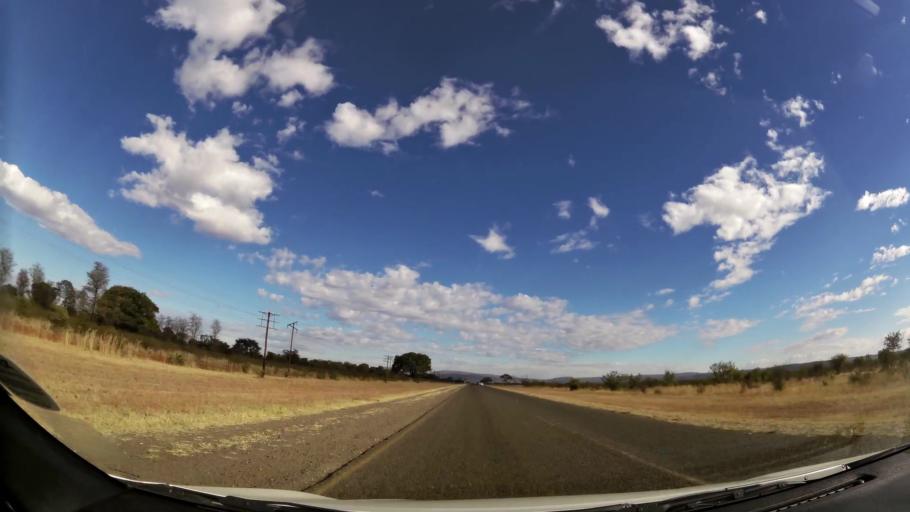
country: ZA
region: Limpopo
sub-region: Waterberg District Municipality
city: Bela-Bela
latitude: -24.9046
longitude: 28.3385
